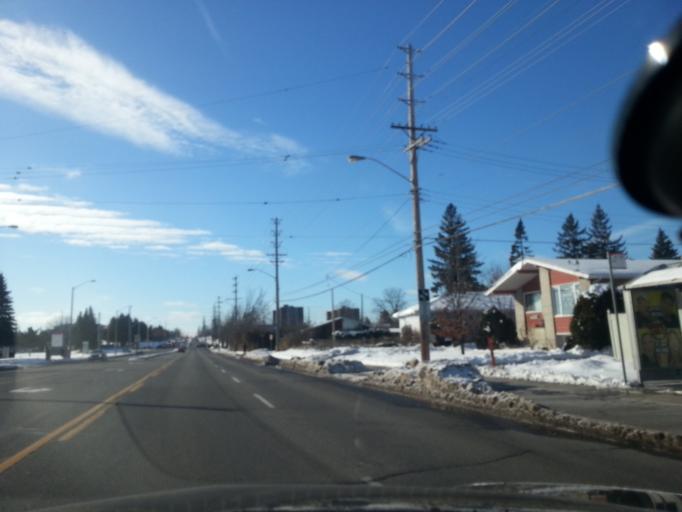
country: CA
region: Ontario
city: Ottawa
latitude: 45.3901
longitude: -75.6147
